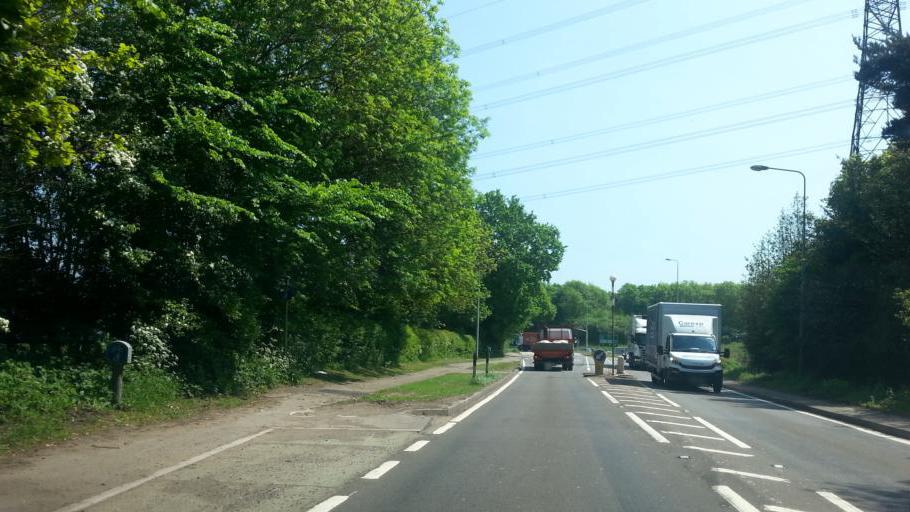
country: GB
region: England
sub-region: Leicestershire
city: Hinckley
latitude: 52.5167
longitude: -1.3650
